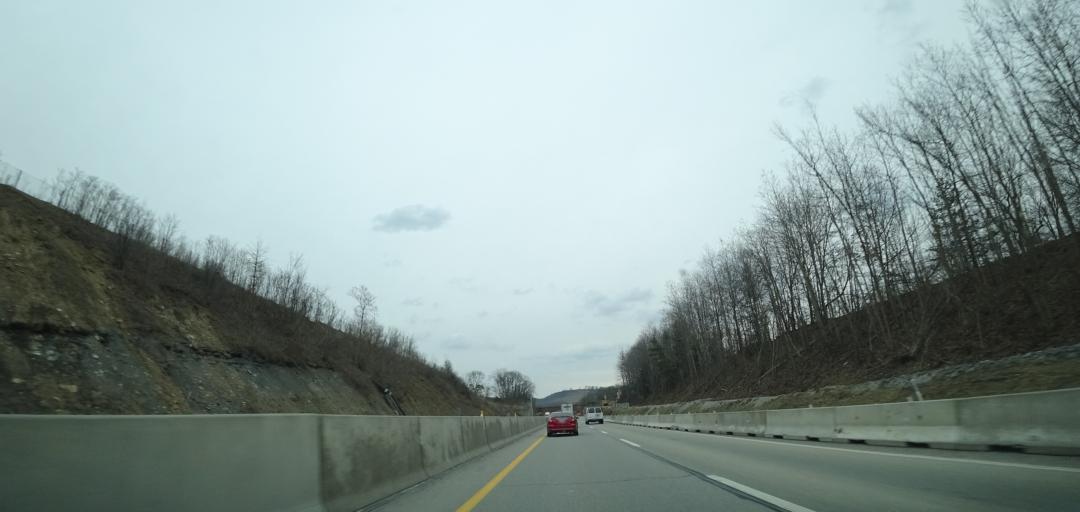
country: US
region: Pennsylvania
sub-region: Beaver County
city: Big Beaver
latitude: 40.8173
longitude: -80.3313
